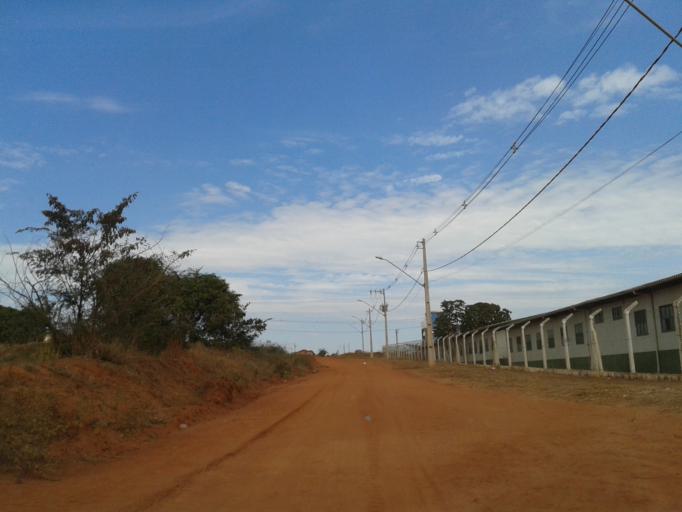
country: BR
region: Minas Gerais
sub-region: Santa Vitoria
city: Santa Vitoria
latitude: -18.8513
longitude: -50.1368
